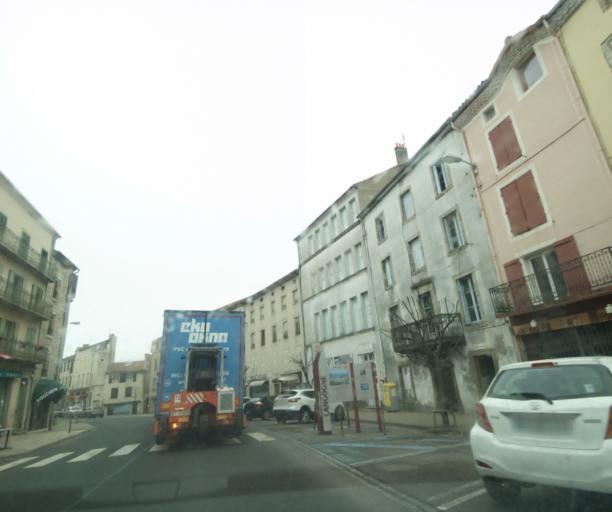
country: FR
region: Languedoc-Roussillon
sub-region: Departement de la Lozere
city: Langogne
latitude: 44.7263
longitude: 3.8558
